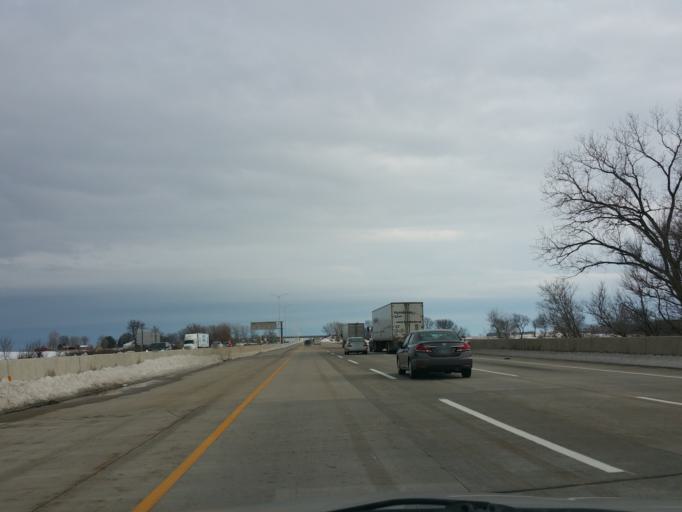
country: US
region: Illinois
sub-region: Boone County
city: Belvidere
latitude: 42.2290
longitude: -88.7735
